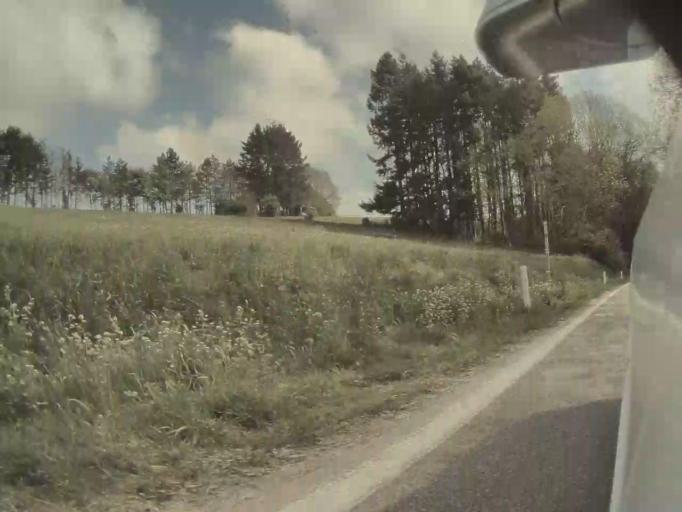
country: BE
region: Wallonia
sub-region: Province du Luxembourg
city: Tellin
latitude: 50.0745
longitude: 5.2007
